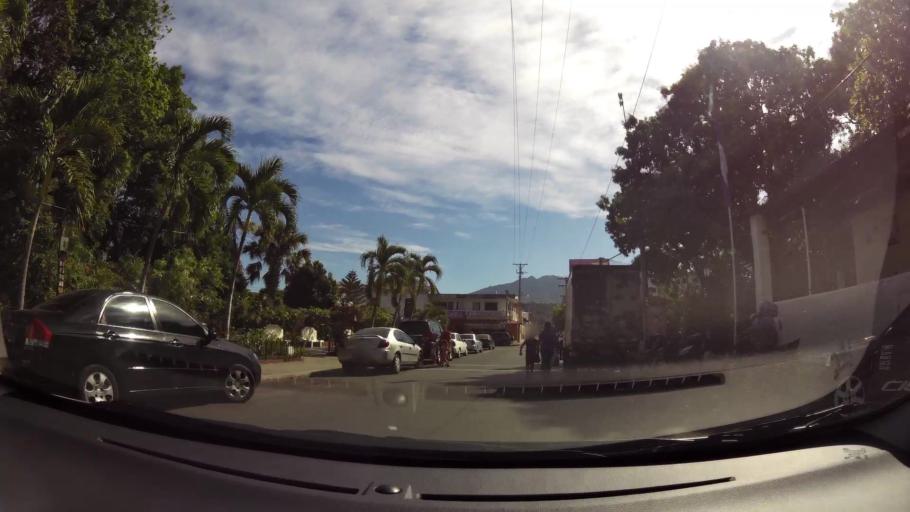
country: SV
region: Santa Ana
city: Chalchuapa
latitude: 13.9855
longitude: -89.6806
